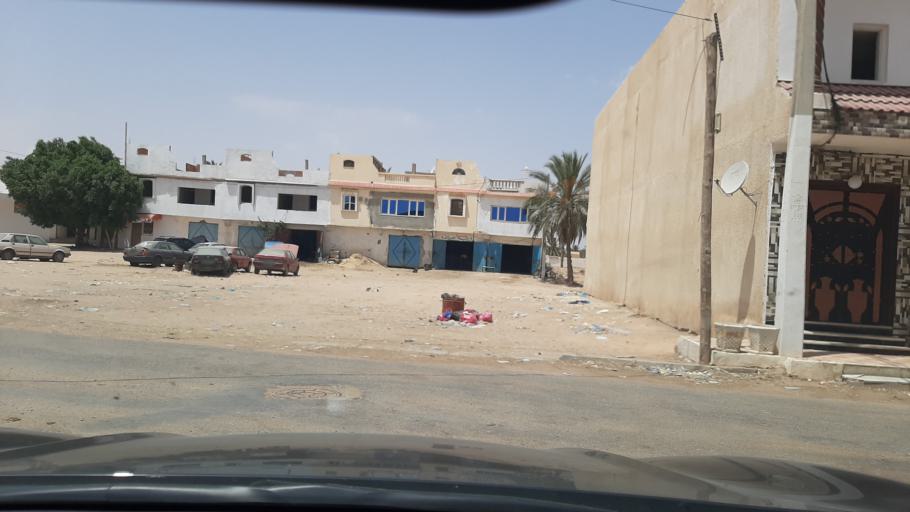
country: TN
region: Qabis
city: Gabes
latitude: 33.6197
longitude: 10.2900
